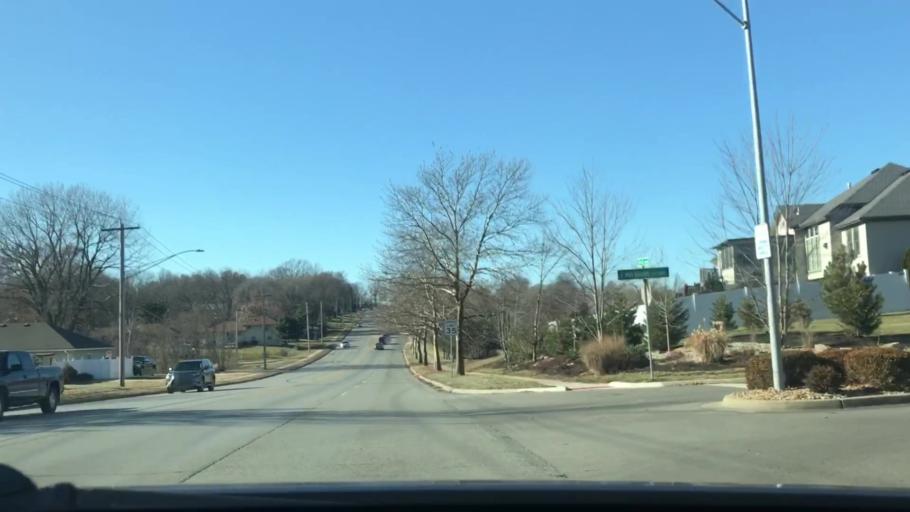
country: US
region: Missouri
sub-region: Jackson County
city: East Independence
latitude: 39.0488
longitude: -94.3804
